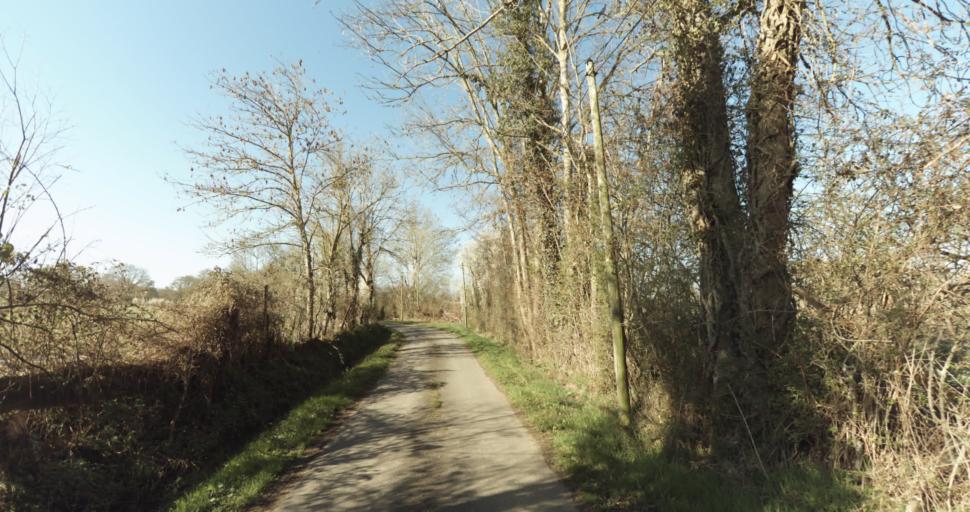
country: FR
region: Lower Normandy
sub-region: Departement du Calvados
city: Saint-Pierre-sur-Dives
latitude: 48.9724
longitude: 0.0352
